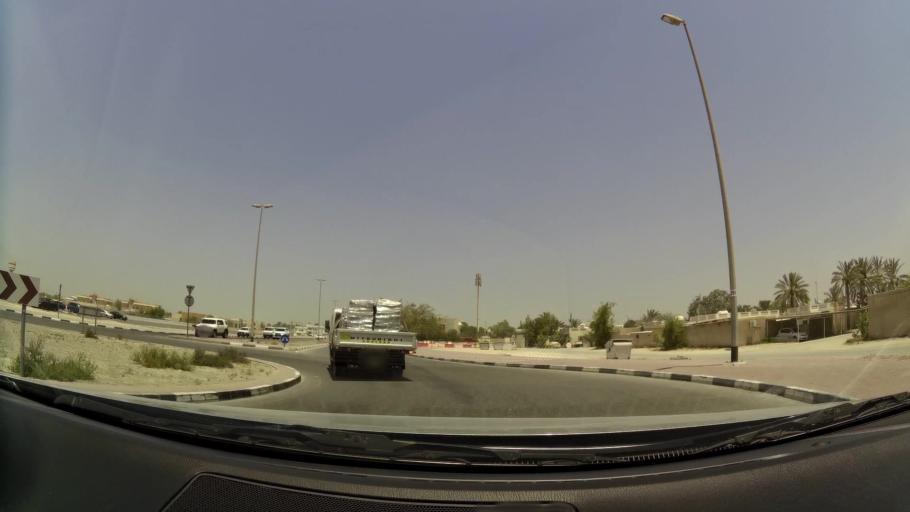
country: AE
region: Dubai
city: Dubai
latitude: 25.1937
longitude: 55.2557
